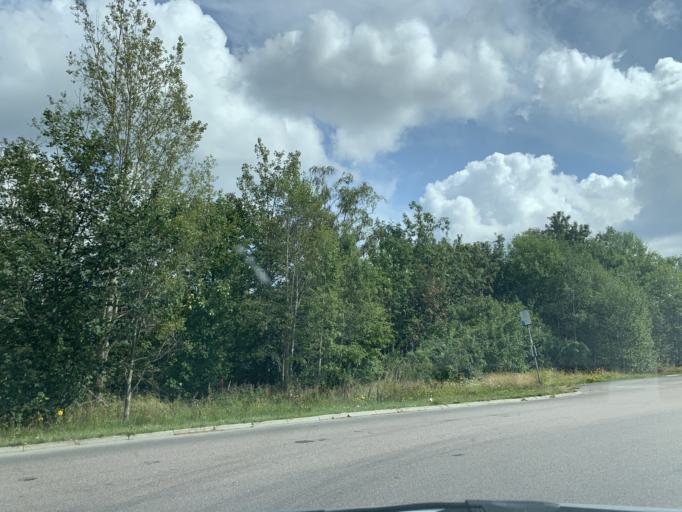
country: SE
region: Vaestra Goetaland
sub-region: Goteborg
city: Eriksbo
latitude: 57.7559
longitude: 12.0476
